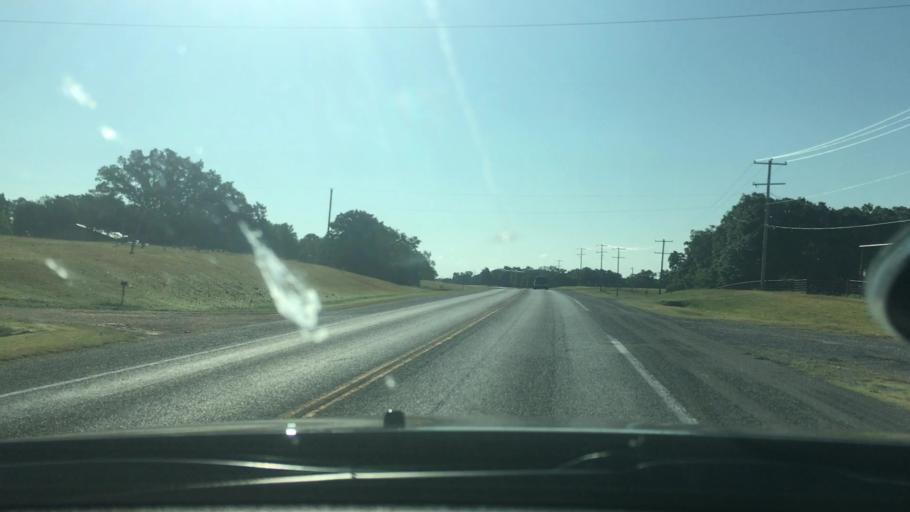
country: US
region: Oklahoma
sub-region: Johnston County
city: Tishomingo
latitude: 34.2377
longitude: -96.7334
